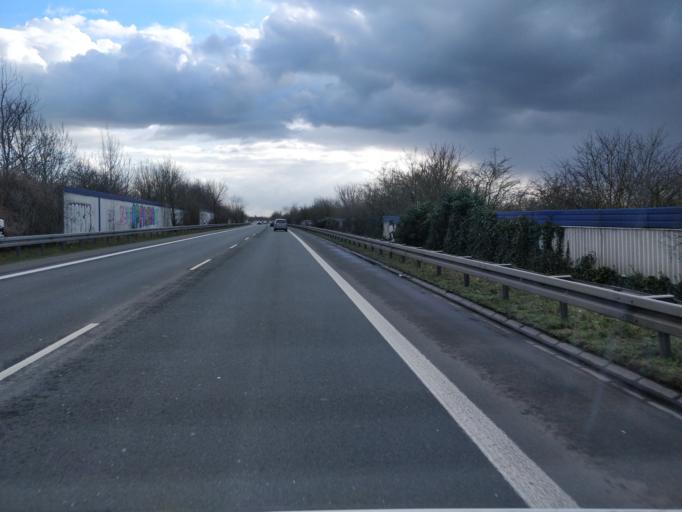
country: DE
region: North Rhine-Westphalia
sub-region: Regierungsbezirk Dusseldorf
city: Bocholt
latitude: 51.8293
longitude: 6.5979
